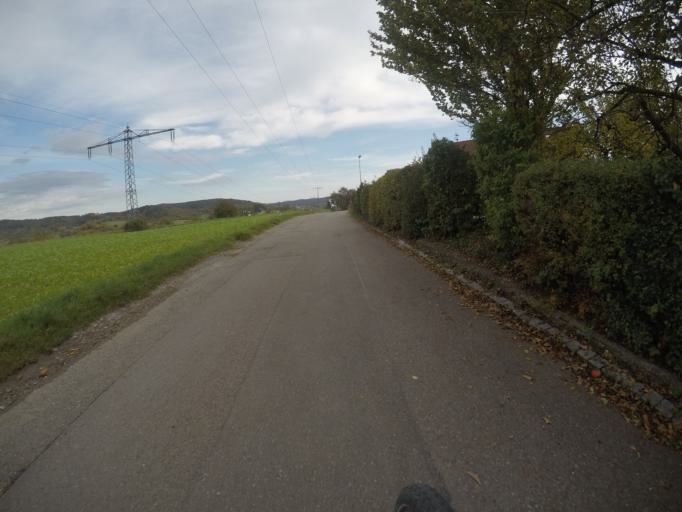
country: DE
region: Baden-Wuerttemberg
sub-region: Tuebingen Region
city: Rottenburg
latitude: 48.5370
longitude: 8.9515
